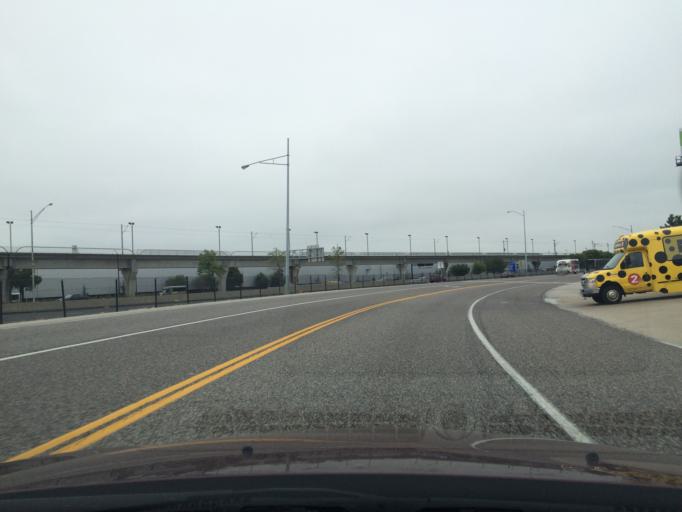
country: US
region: Missouri
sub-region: Saint Louis County
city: Woodson Terrace
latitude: 38.7385
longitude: -90.3640
